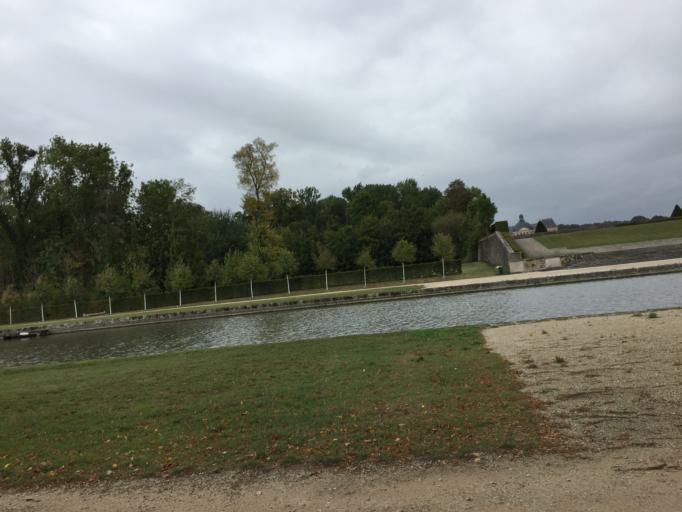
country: FR
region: Ile-de-France
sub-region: Departement de Seine-et-Marne
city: Maincy
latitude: 48.5598
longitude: 2.7139
